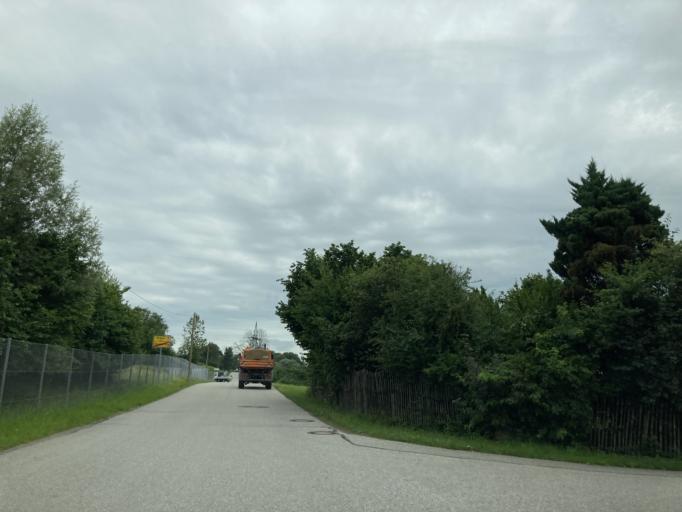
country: DE
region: Bavaria
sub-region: Upper Bavaria
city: Stephanskirchen
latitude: 47.8688
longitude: 12.1694
